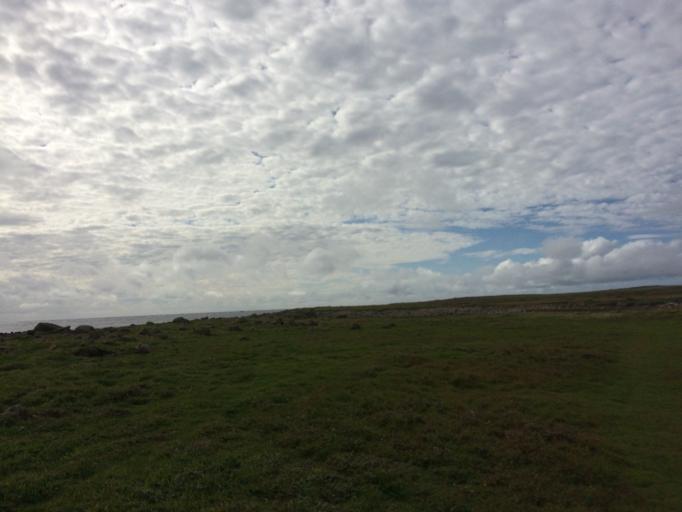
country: IE
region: Ulster
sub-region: County Donegal
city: Derrybeg
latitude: 55.2542
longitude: -8.1975
